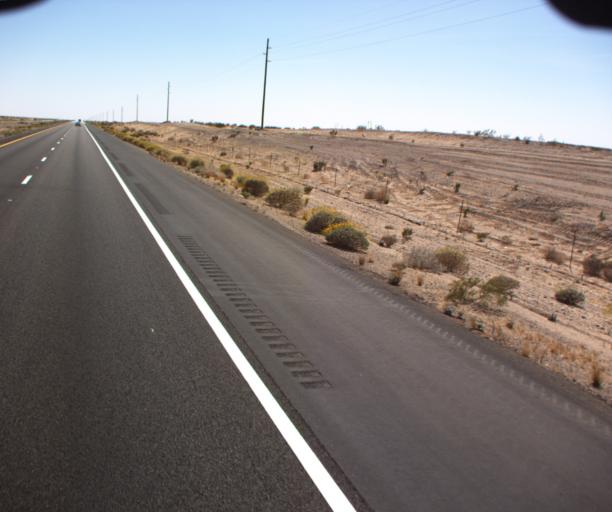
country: US
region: Arizona
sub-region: Yuma County
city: Somerton
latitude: 32.5393
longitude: -114.5623
